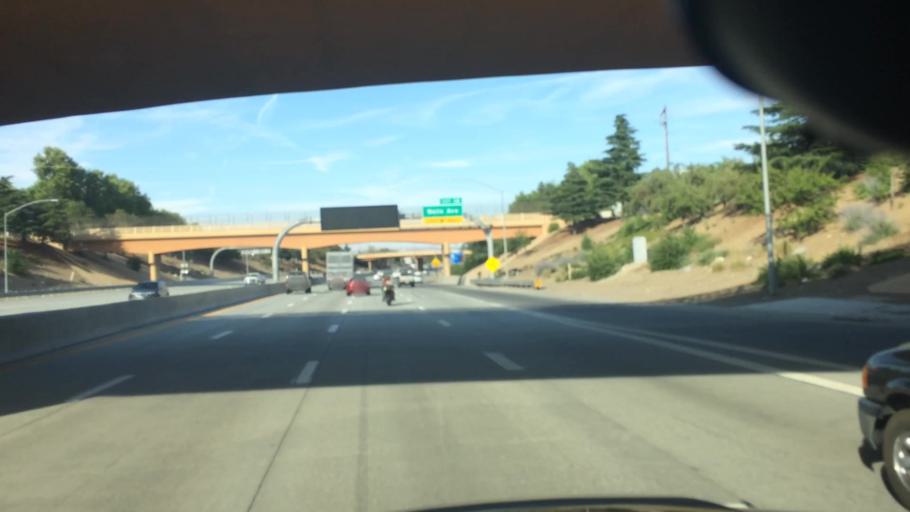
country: US
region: Nevada
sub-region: Washoe County
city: Reno
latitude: 39.5355
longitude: -119.8120
